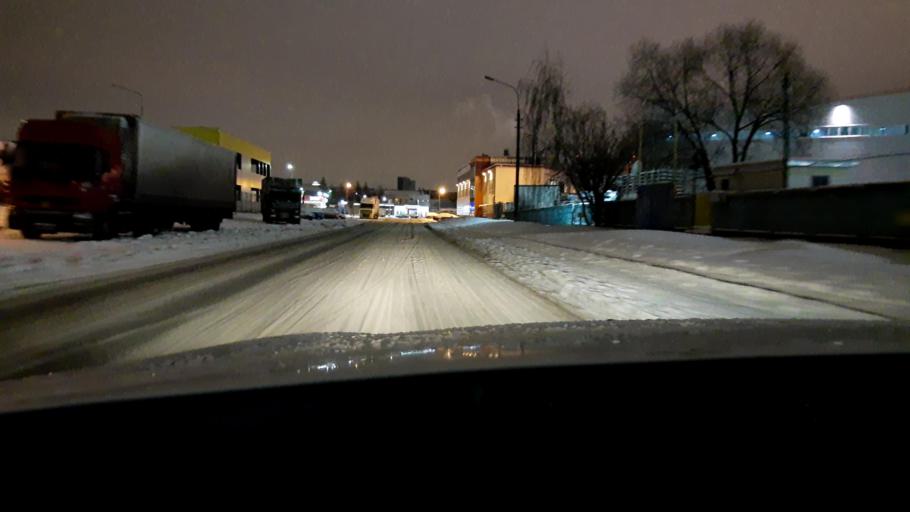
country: RU
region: Moscow
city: Khimki
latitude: 55.9139
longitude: 37.4167
